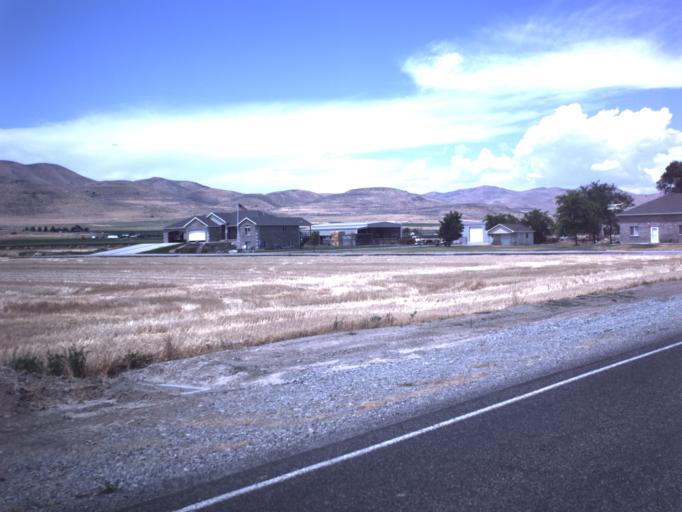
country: US
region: Utah
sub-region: Box Elder County
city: Tremonton
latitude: 41.7002
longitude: -112.2779
